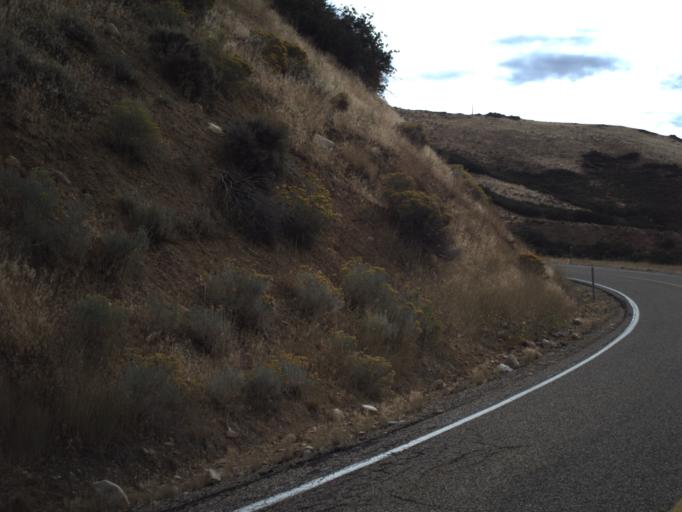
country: US
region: Utah
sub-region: Morgan County
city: Morgan
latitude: 40.9241
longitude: -111.6094
